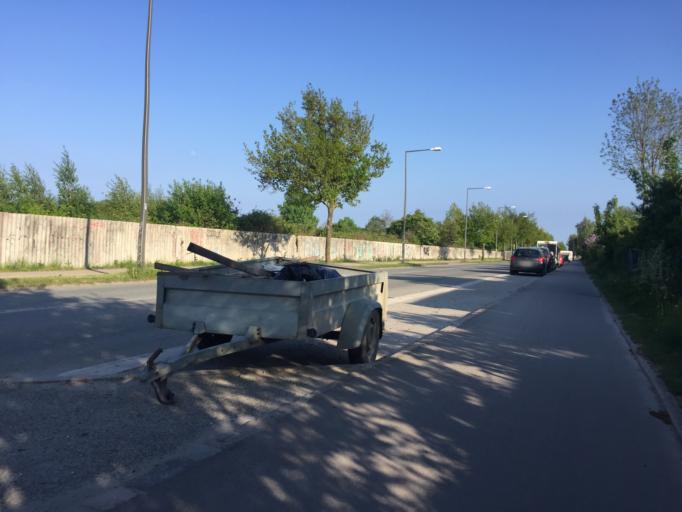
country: DK
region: Capital Region
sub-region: Kobenhavn
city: Christianshavn
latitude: 55.6813
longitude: 12.6151
